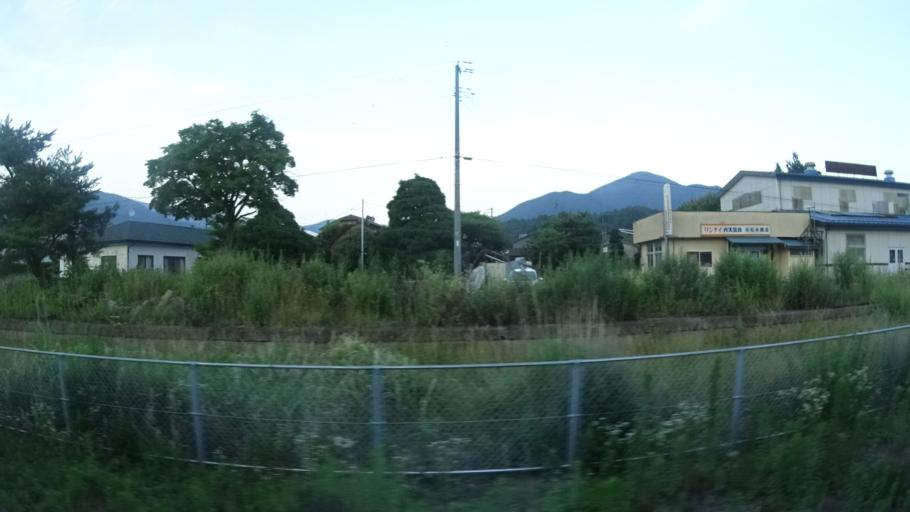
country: JP
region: Fukushima
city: Funehikimachi-funehiki
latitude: 37.3250
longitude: 140.6597
